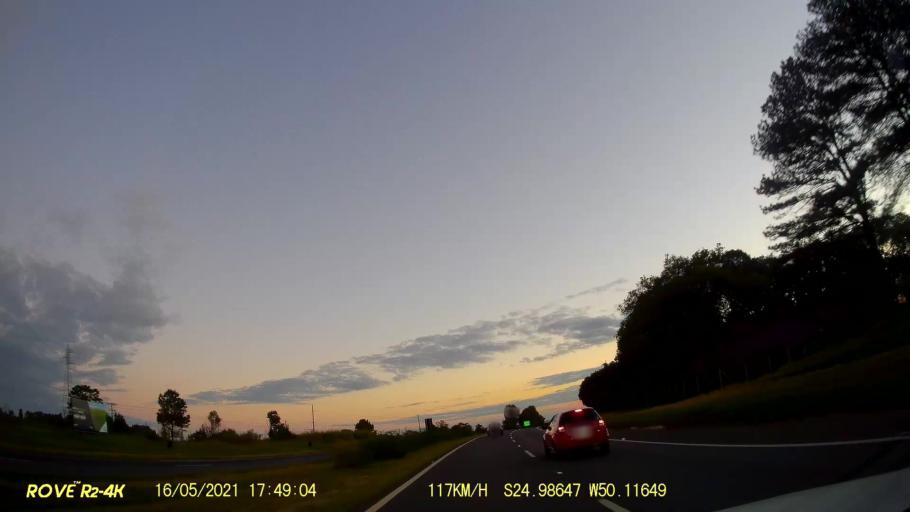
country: BR
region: Parana
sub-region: Carambei
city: Carambei
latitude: -24.9863
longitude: -50.1170
